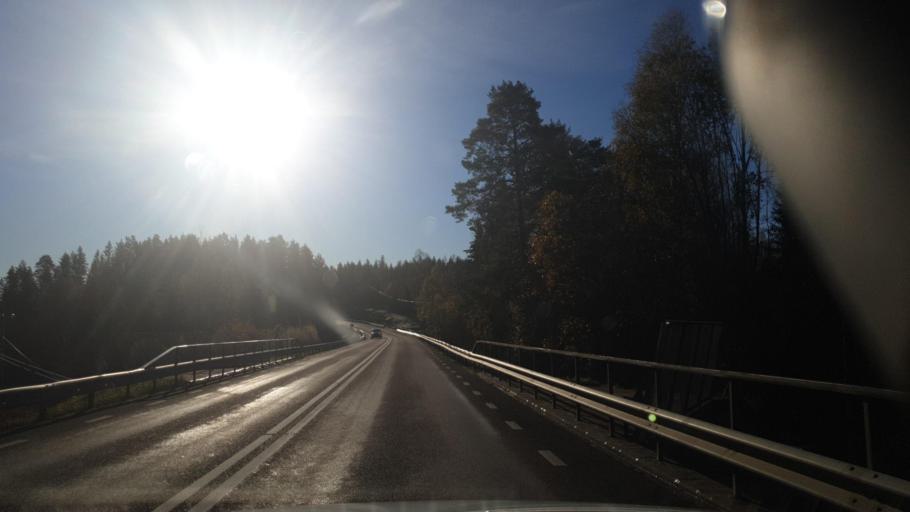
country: SE
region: Vaermland
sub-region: Karlstads Kommun
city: Edsvalla
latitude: 59.6097
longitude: 12.9889
